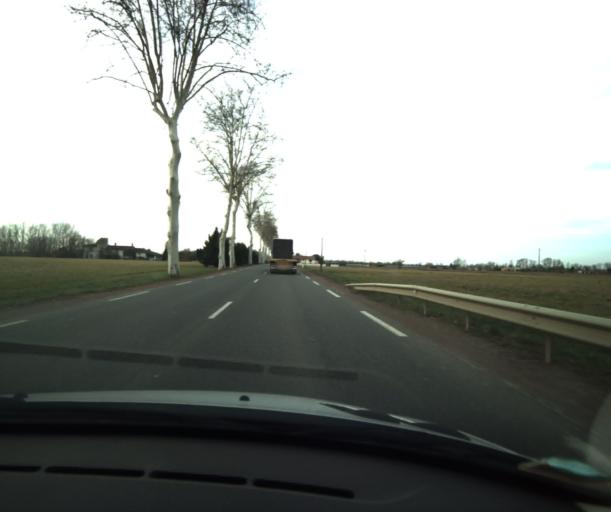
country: FR
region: Midi-Pyrenees
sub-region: Departement du Tarn-et-Garonne
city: Saint-Porquier
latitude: 44.0165
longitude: 1.1641
